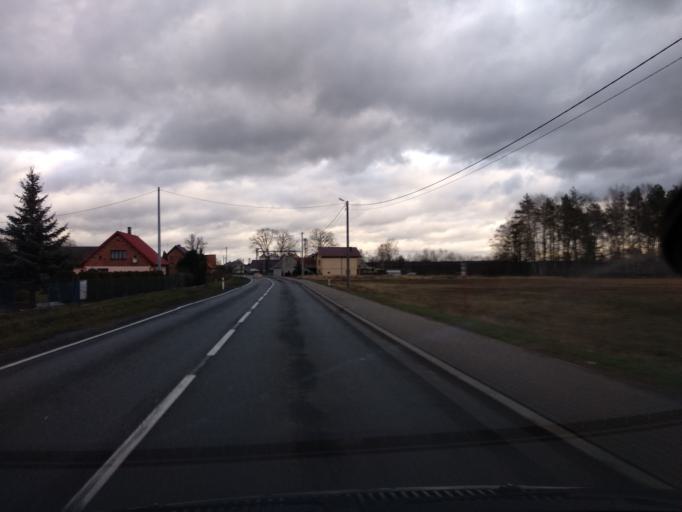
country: PL
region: Lower Silesian Voivodeship
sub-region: Powiat olesnicki
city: Miedzyborz
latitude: 51.4355
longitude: 17.6941
